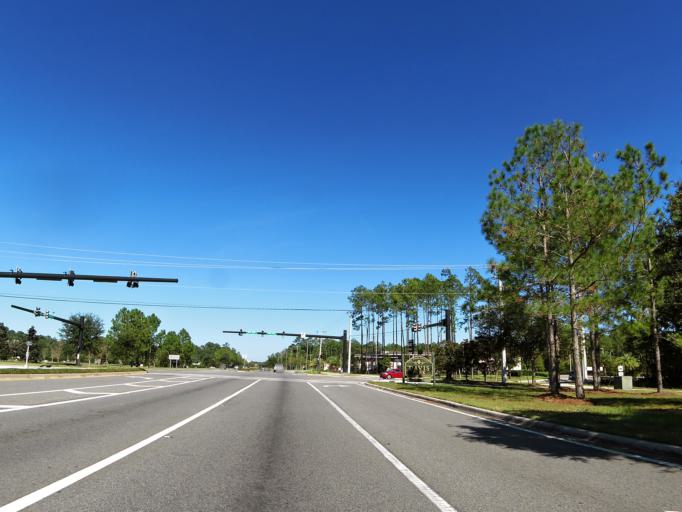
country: US
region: Florida
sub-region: Saint Johns County
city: Palm Valley
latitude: 30.1228
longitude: -81.4000
